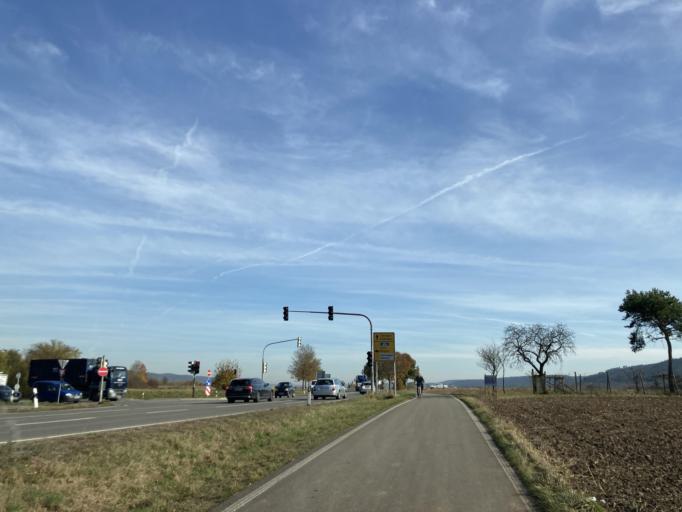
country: DE
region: Baden-Wuerttemberg
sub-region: Tuebingen Region
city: Rottenburg
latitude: 48.4712
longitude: 8.9539
